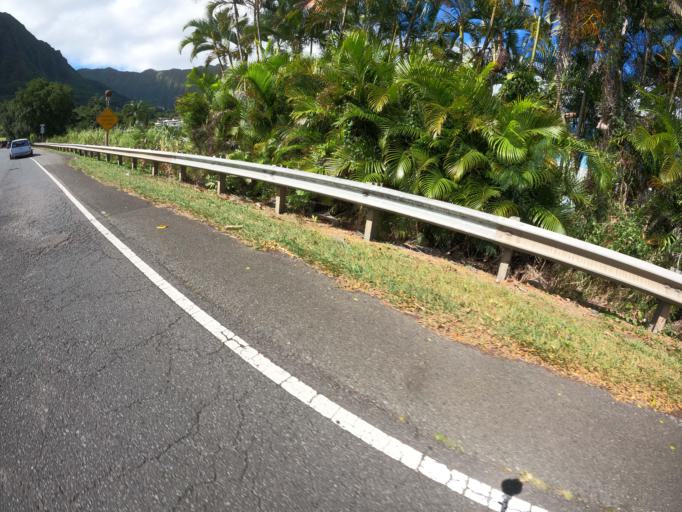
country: US
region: Hawaii
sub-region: Honolulu County
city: Kane'ohe
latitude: 21.4038
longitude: -157.8053
